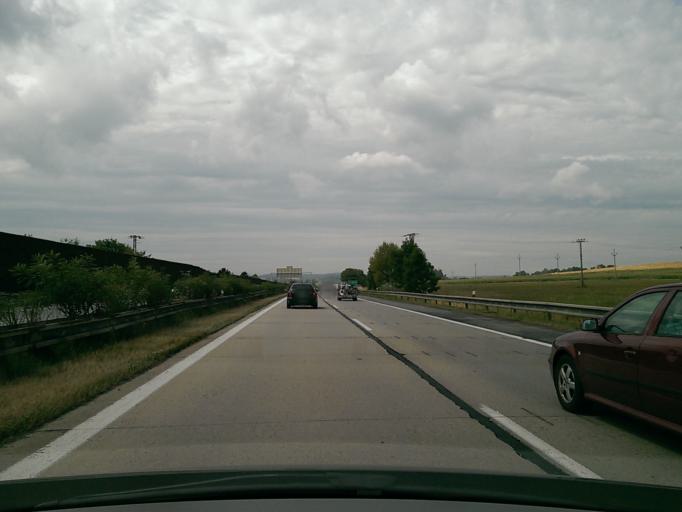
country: CZ
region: Vysocina
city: Merin
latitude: 49.3980
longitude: 15.8766
